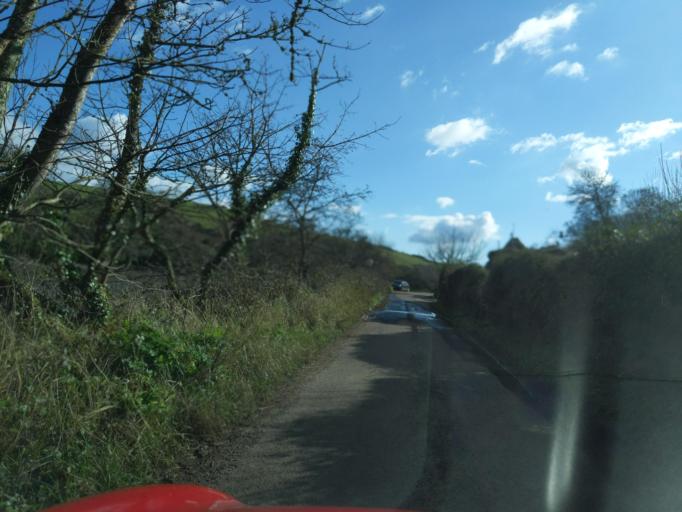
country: GB
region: England
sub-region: Devon
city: Kingsbridge
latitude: 50.2825
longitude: -3.7596
